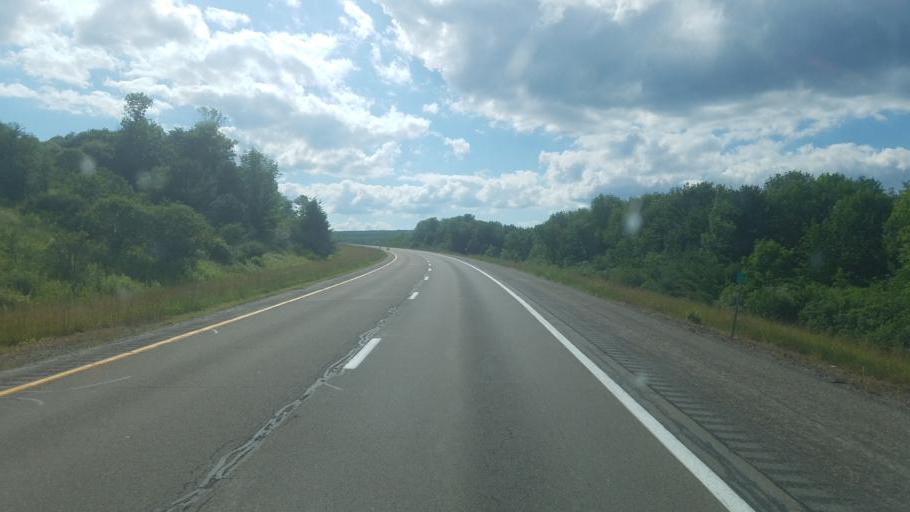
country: US
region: New York
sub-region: Allegany County
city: Alfred
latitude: 42.3198
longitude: -77.8279
